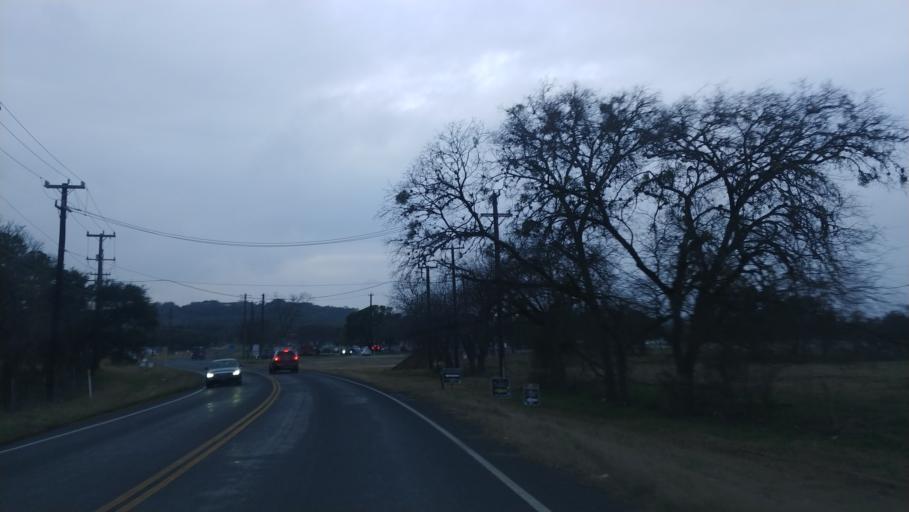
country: US
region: Texas
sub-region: Bexar County
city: Scenic Oaks
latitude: 29.6811
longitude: -98.6727
